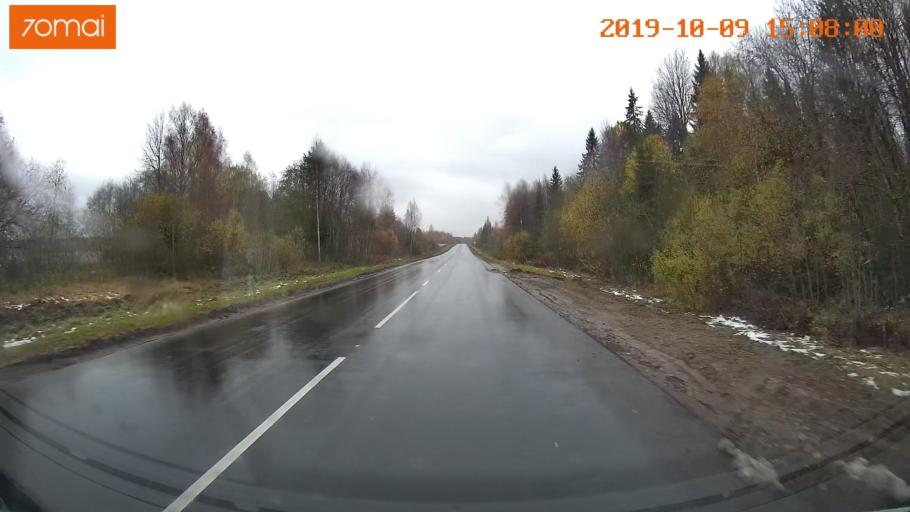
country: RU
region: Kostroma
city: Susanino
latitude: 58.2120
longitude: 41.6470
